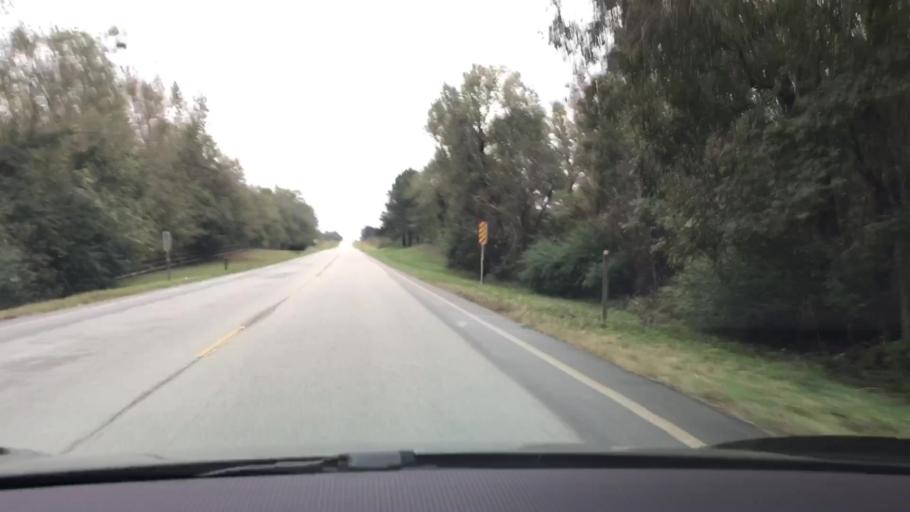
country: US
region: Georgia
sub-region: Jefferson County
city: Wrens
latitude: 33.2373
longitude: -82.4566
